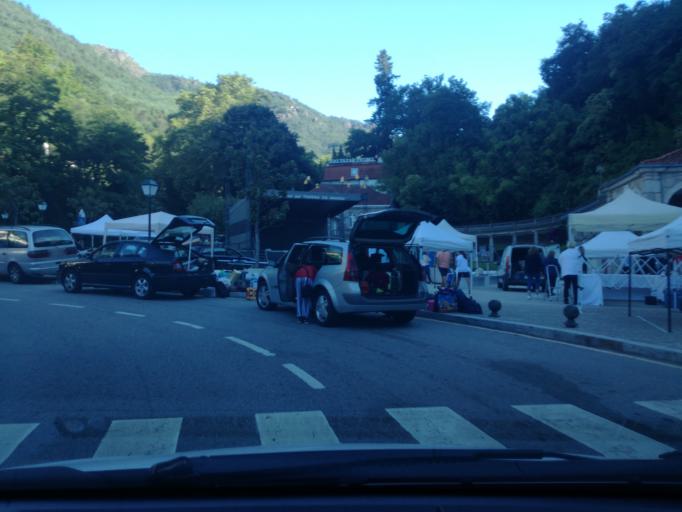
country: PT
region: Braga
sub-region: Vieira do Minho
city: Real
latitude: 41.7293
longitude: -8.1615
